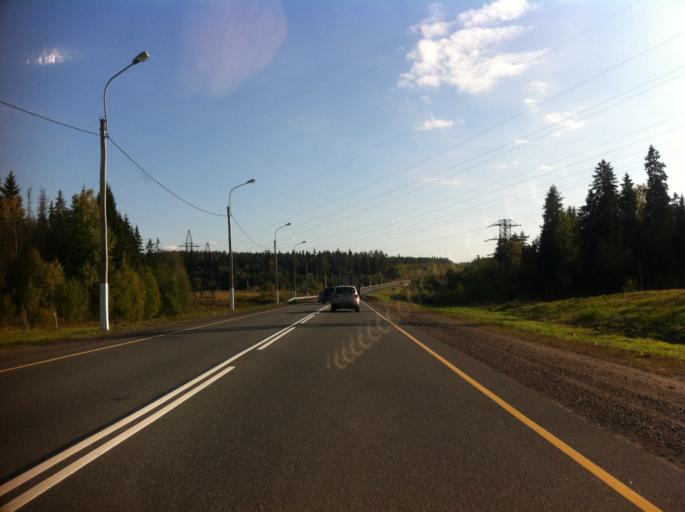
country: RU
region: Leningrad
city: Luga
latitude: 58.7568
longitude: 29.8881
